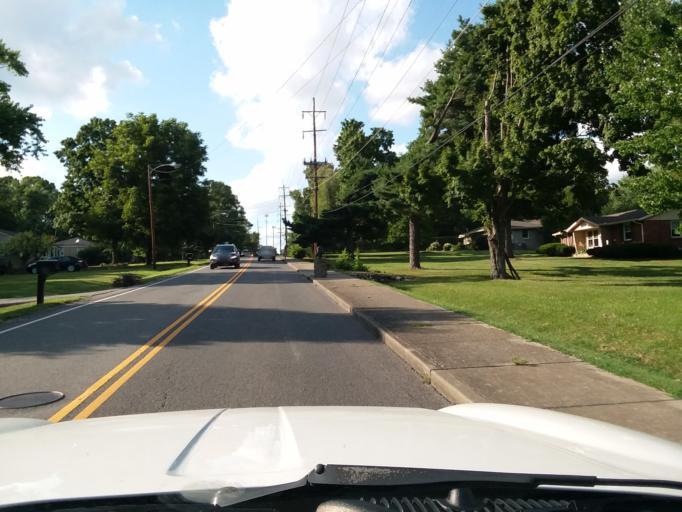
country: US
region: Tennessee
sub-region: Davidson County
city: Oak Hill
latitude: 36.0718
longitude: -86.7588
